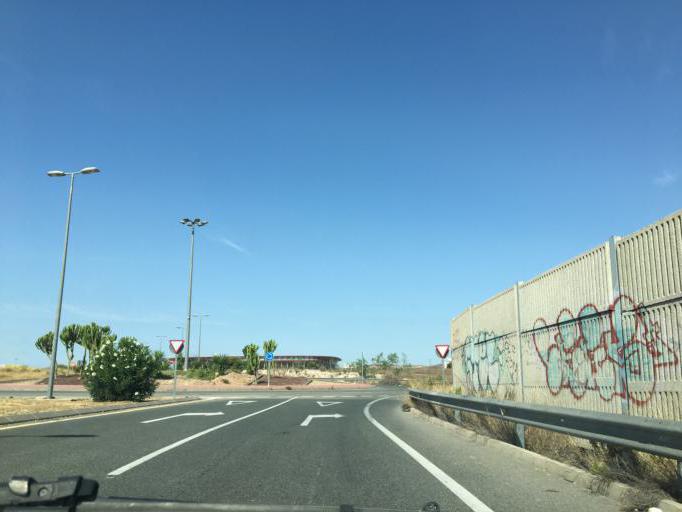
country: ES
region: Murcia
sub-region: Murcia
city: Murcia
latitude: 38.0436
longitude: -1.1360
